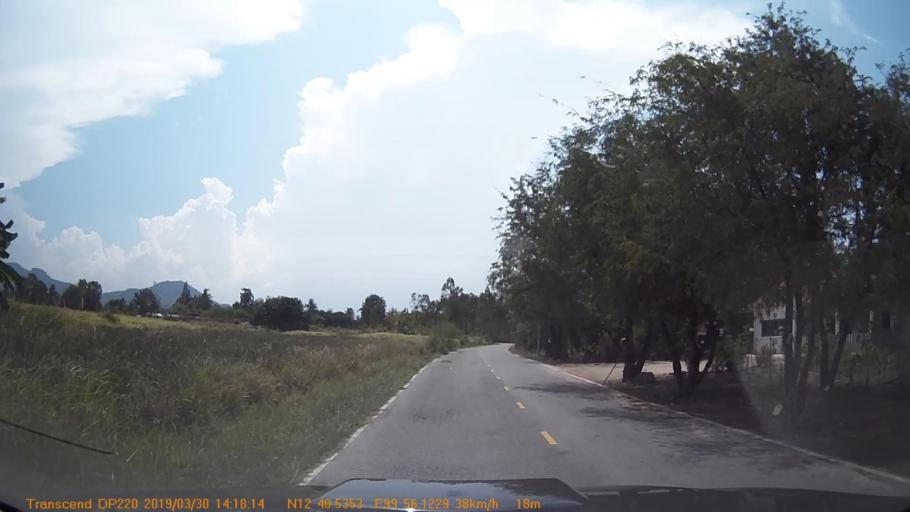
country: TH
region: Prachuap Khiri Khan
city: Hua Hin
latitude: 12.6756
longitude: 99.9353
